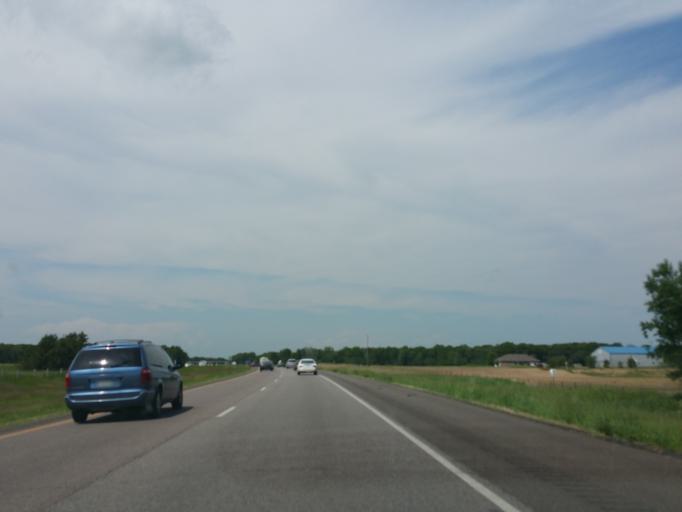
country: US
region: Minnesota
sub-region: Chisago County
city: Stacy
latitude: 45.4379
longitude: -92.9893
